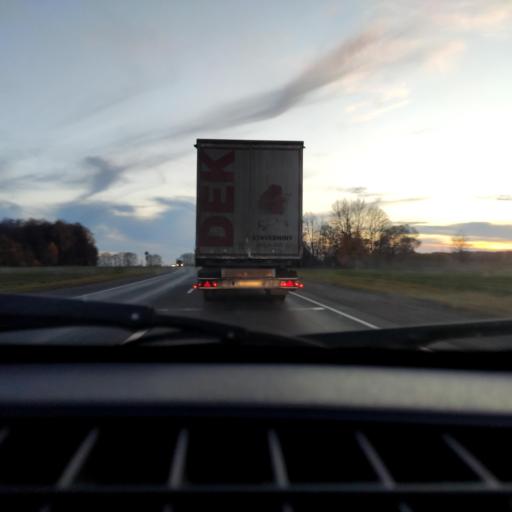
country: RU
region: Bashkortostan
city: Avdon
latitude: 54.6904
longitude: 55.7476
